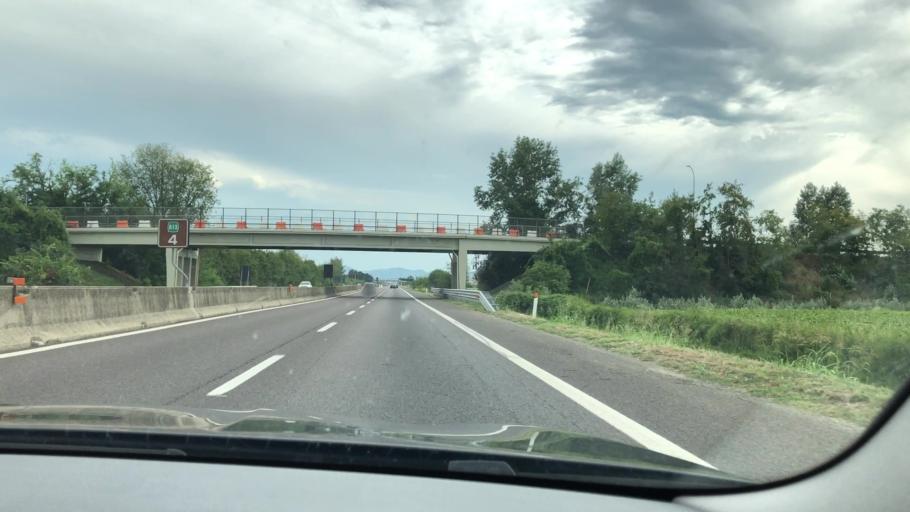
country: IT
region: Emilia-Romagna
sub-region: Provincia di Bologna
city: Progresso
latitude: 44.5707
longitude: 11.3865
